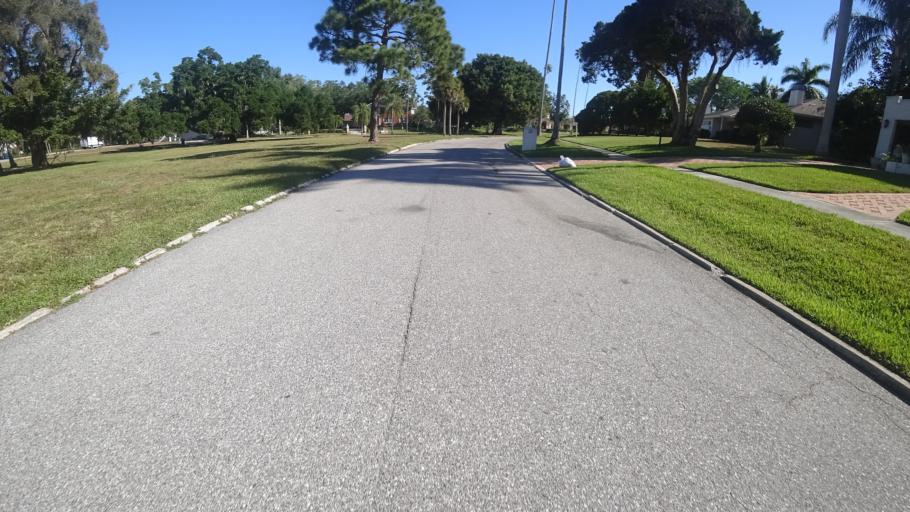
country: US
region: Florida
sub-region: Manatee County
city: West Bradenton
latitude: 27.4942
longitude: -82.6429
